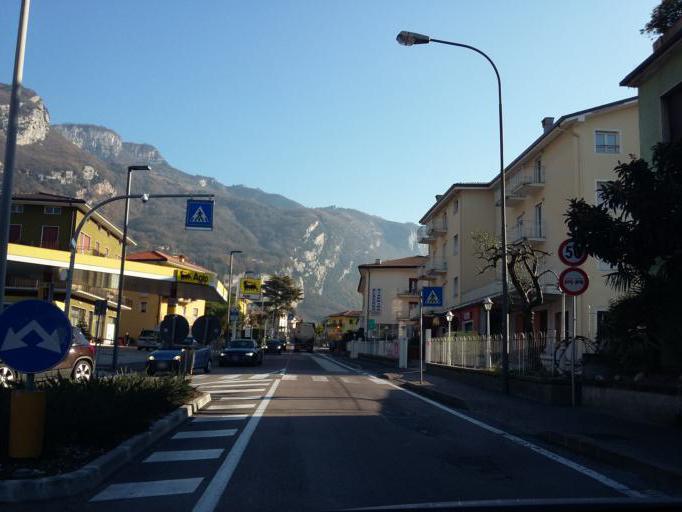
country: IT
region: Trentino-Alto Adige
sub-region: Provincia di Trento
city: Nago-Torbole
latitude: 45.8784
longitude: 10.8891
